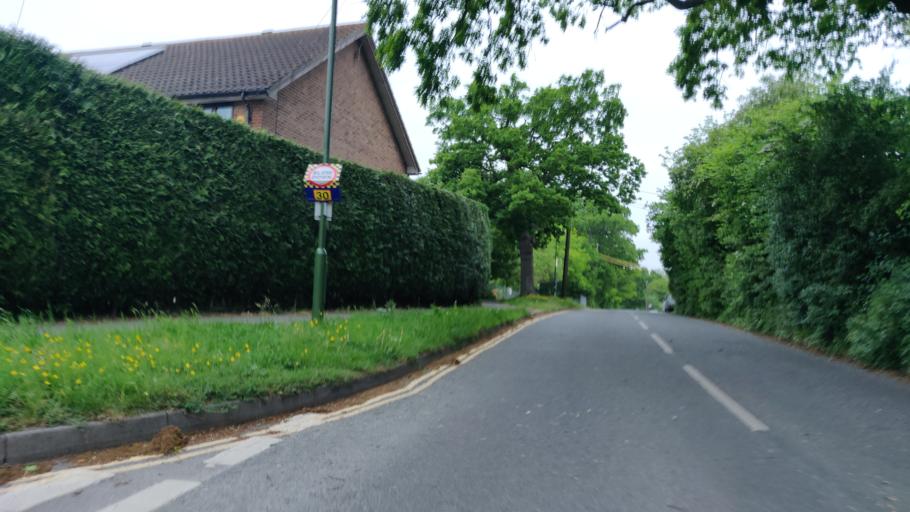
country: GB
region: England
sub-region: West Sussex
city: Partridge Green
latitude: 50.9619
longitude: -0.3023
